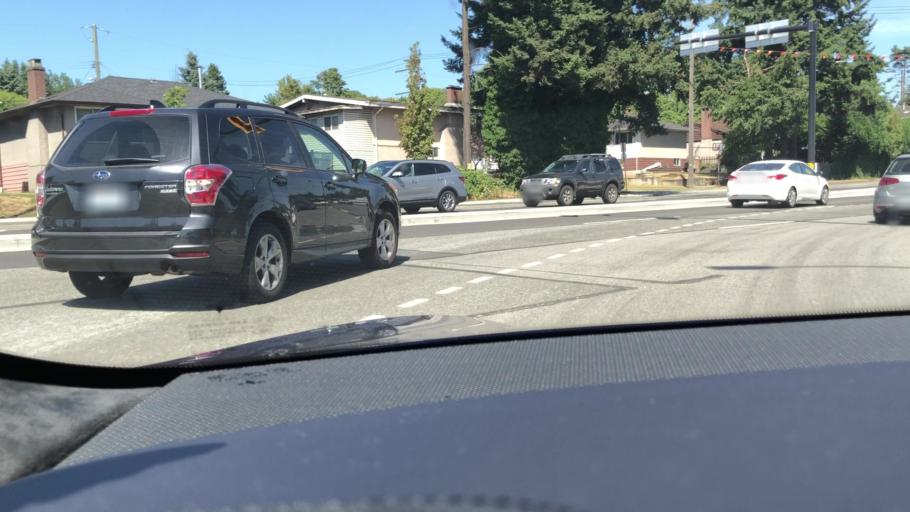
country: CA
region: British Columbia
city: Vancouver
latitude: 49.2110
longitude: -123.0748
